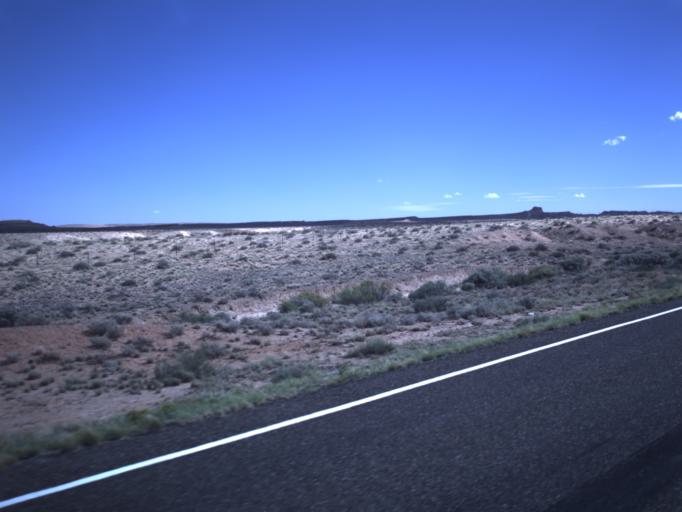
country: US
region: Utah
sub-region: Emery County
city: Ferron
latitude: 38.2973
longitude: -110.6679
